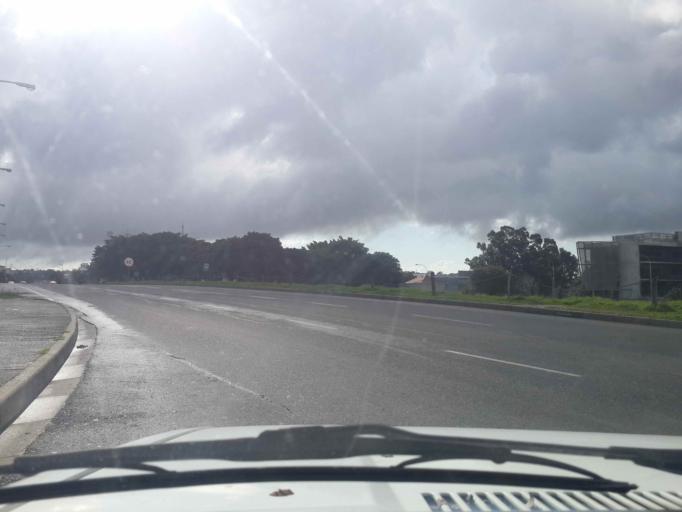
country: ZA
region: Western Cape
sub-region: City of Cape Town
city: Kraaifontein
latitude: -33.8862
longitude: 18.6342
